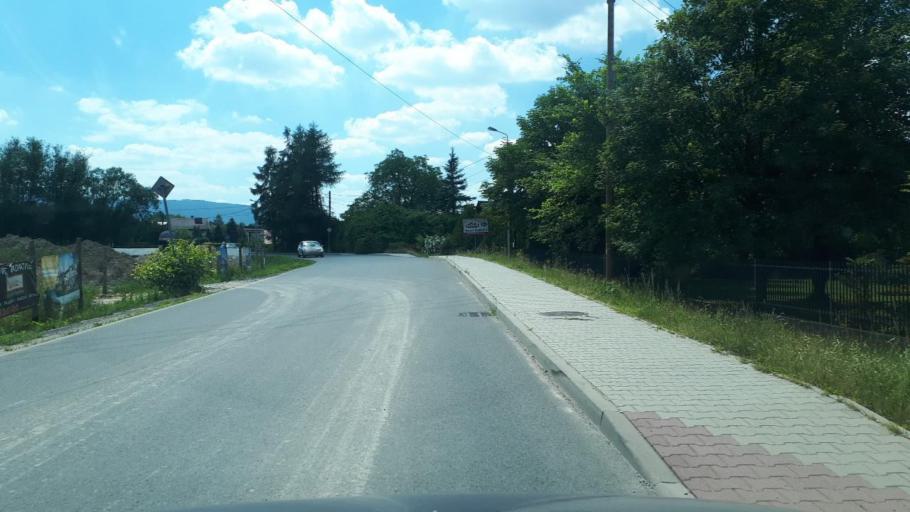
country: PL
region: Silesian Voivodeship
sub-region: Powiat bielski
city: Pisarzowice
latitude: 49.8815
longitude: 19.1441
